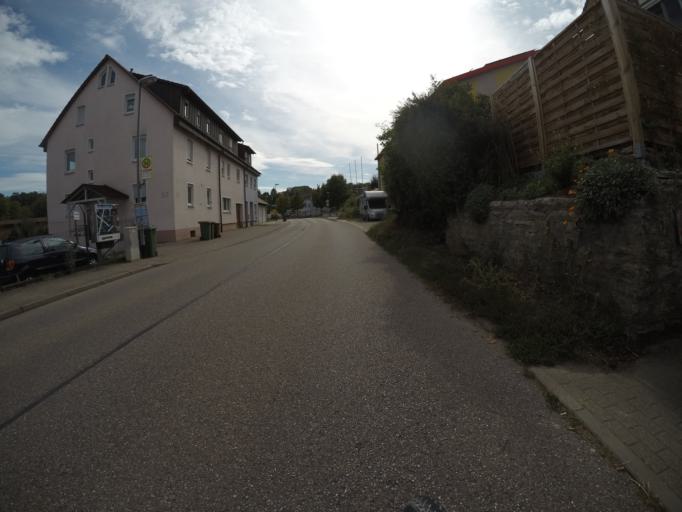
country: DE
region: Baden-Wuerttemberg
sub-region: Regierungsbezirk Stuttgart
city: Vaihingen an der Enz
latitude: 48.9150
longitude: 8.9804
